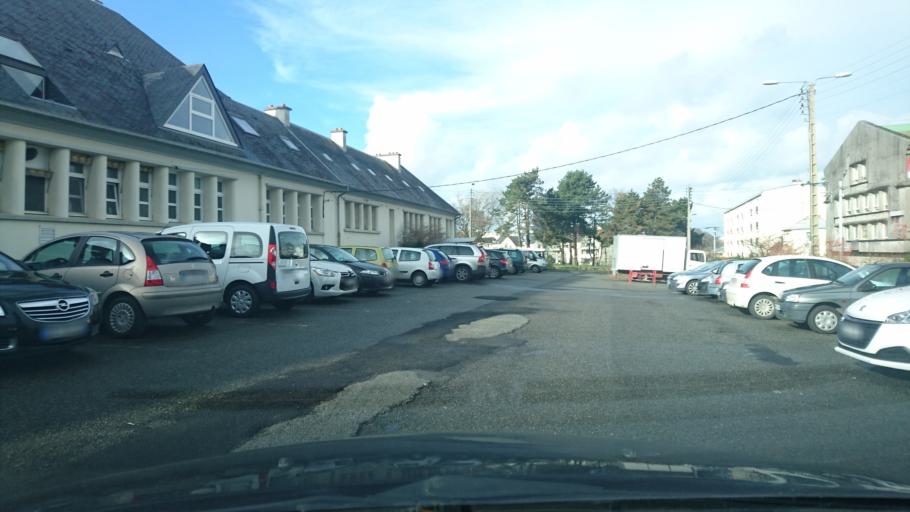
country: FR
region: Brittany
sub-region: Departement du Finistere
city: Brest
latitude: 48.3872
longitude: -4.5035
